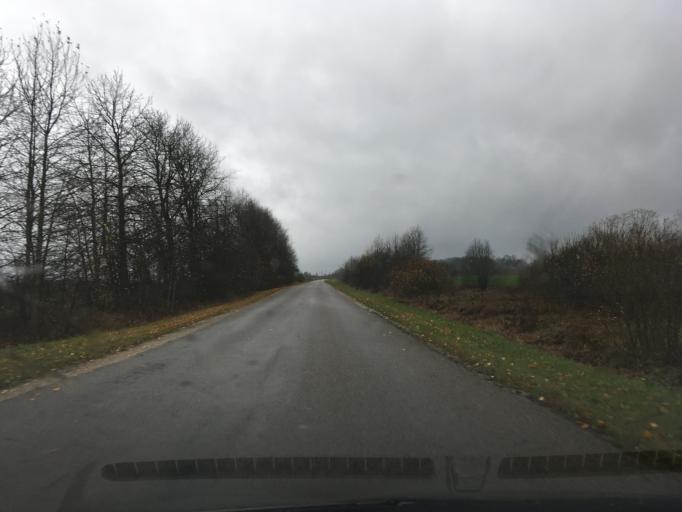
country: EE
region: Laeaene
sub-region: Lihula vald
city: Lihula
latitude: 58.6990
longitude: 23.8548
